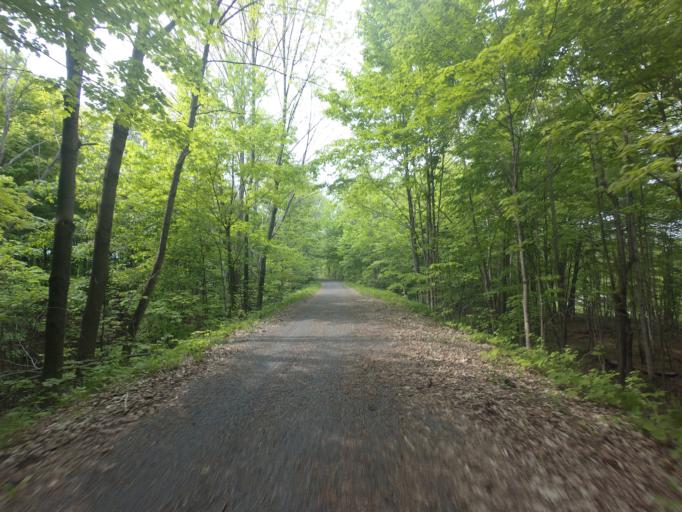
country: CA
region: Ontario
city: Kingston
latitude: 44.4001
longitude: -76.6411
